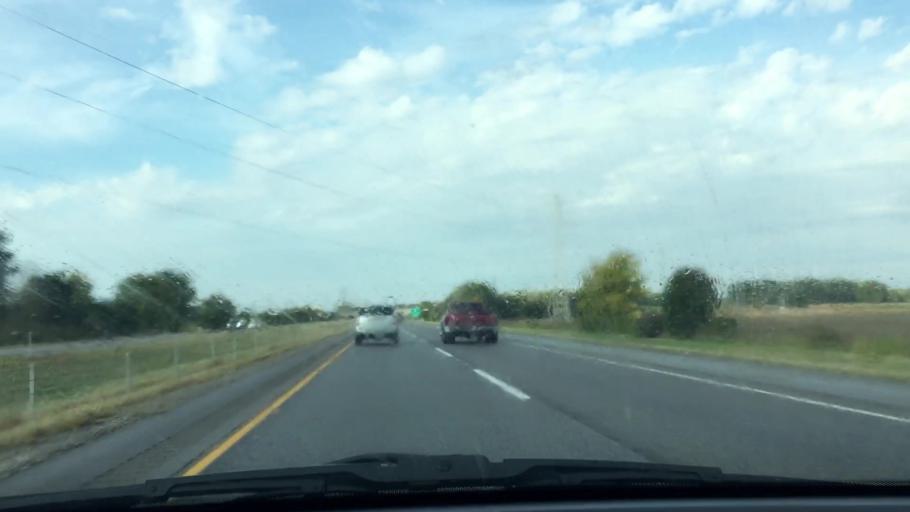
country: US
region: Illinois
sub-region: Whiteside County
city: Rock Falls
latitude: 41.7700
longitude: -89.5929
